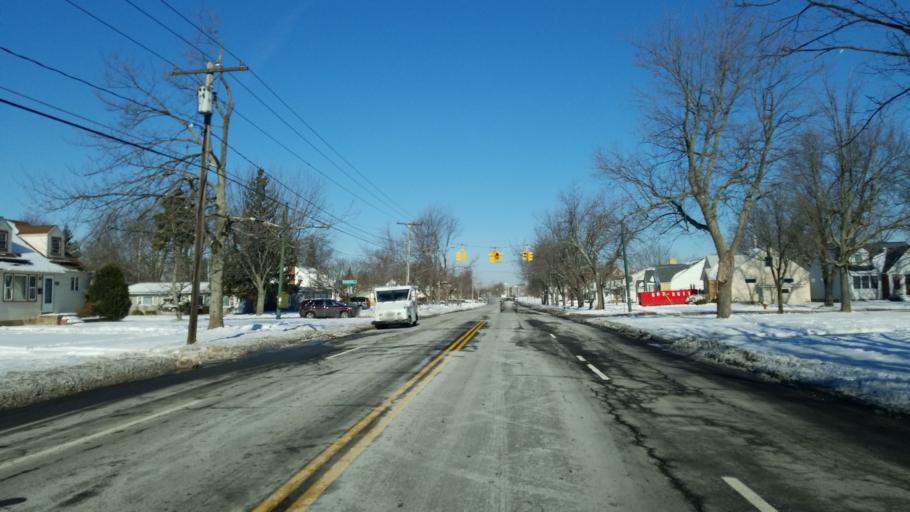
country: US
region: New York
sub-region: Erie County
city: Amherst
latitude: 42.9838
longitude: -78.8296
